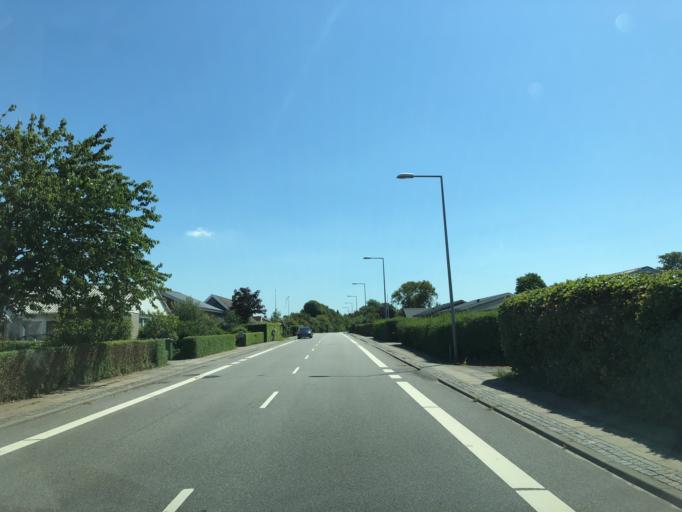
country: DK
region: Central Jutland
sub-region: Holstebro Kommune
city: Holstebro
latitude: 56.3471
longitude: 8.6493
